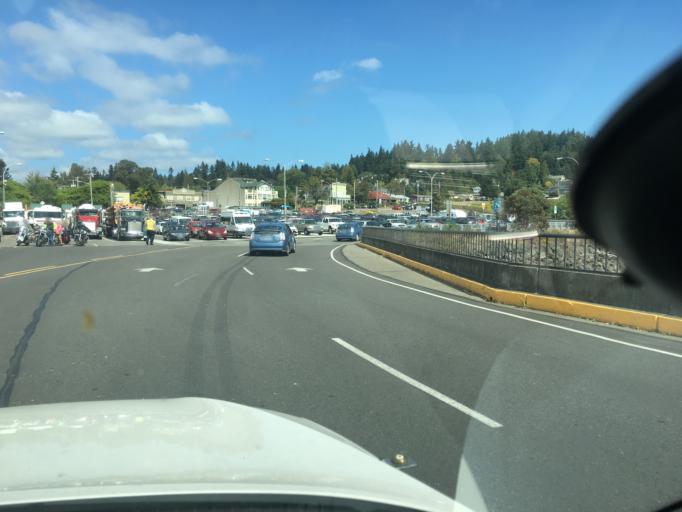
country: US
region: Washington
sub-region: Kitsap County
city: Kingston
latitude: 47.7955
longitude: -122.4958
